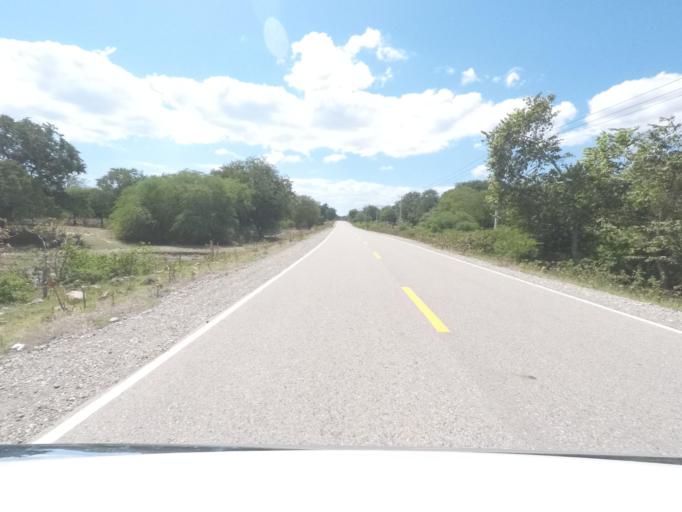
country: TL
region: Lautem
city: Lospalos
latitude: -8.4193
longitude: 126.7860
